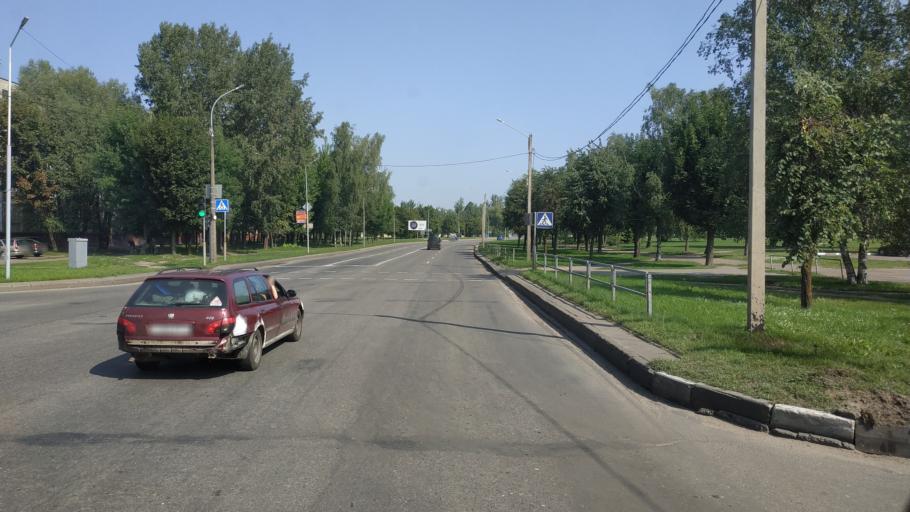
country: BY
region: Mogilev
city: Buynichy
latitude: 53.8731
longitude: 30.3127
